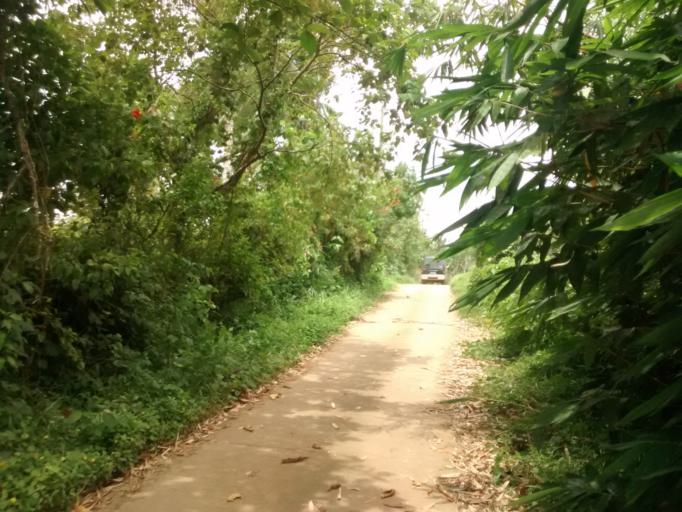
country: PH
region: Calabarzon
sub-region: Province of Quezon
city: Lucban
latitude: 14.1547
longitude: 121.5571
